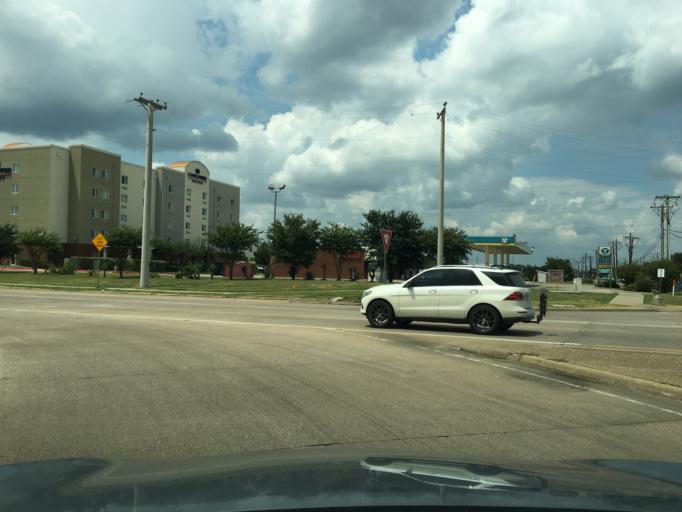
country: US
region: Texas
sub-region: Collin County
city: Plano
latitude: 33.0030
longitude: -96.6826
